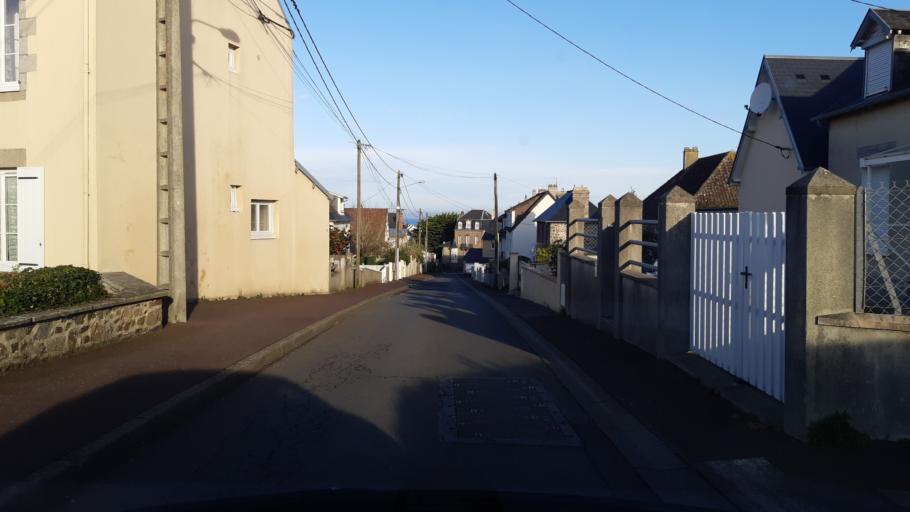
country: FR
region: Lower Normandy
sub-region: Departement de la Manche
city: Donville-les-Bains
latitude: 48.8488
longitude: -1.5733
